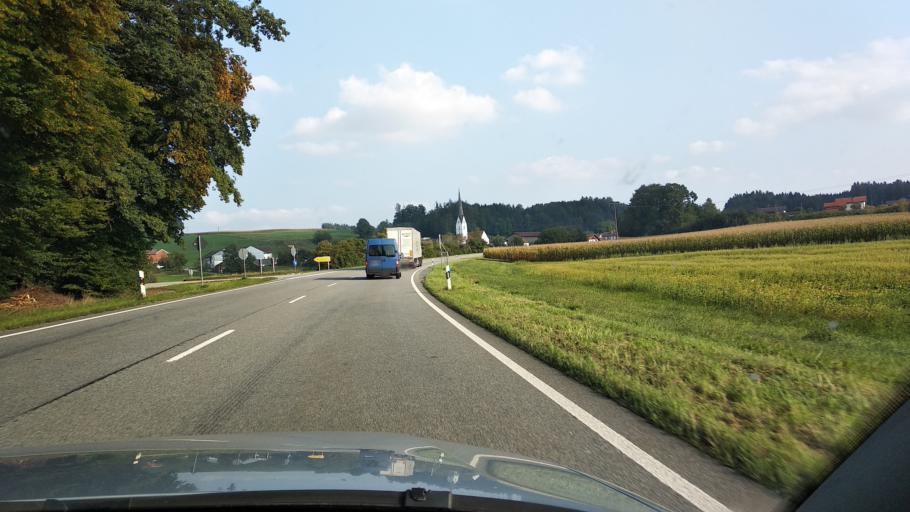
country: DE
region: Bavaria
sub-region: Upper Bavaria
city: Schnaitsee
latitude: 48.0441
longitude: 12.3328
